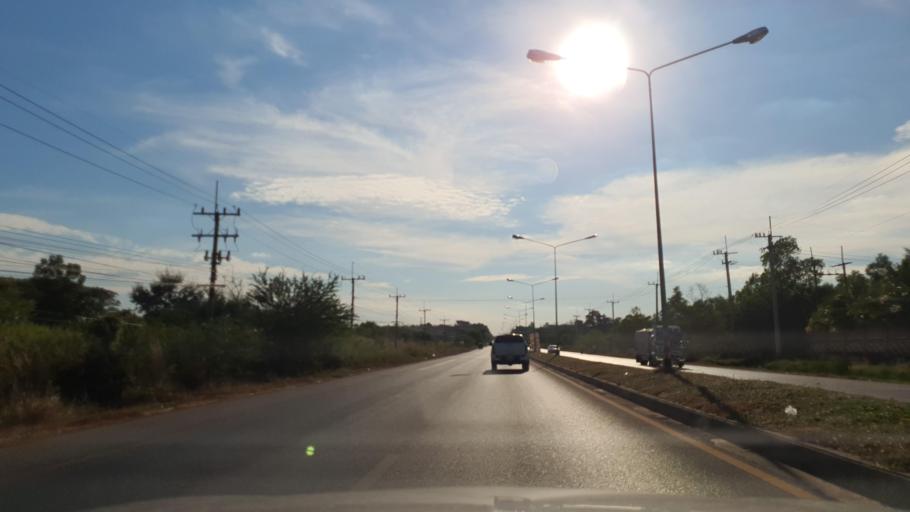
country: TH
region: Maha Sarakham
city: Kantharawichai
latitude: 16.3387
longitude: 103.3122
